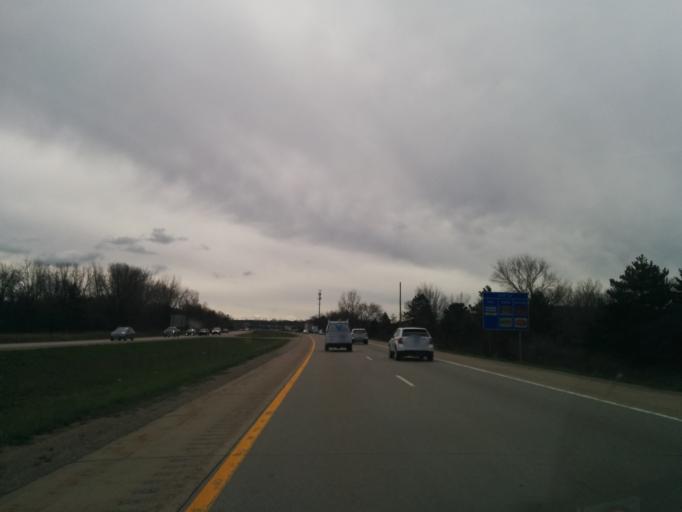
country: US
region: Michigan
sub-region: Ottawa County
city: Jenison
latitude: 42.8962
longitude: -85.7808
